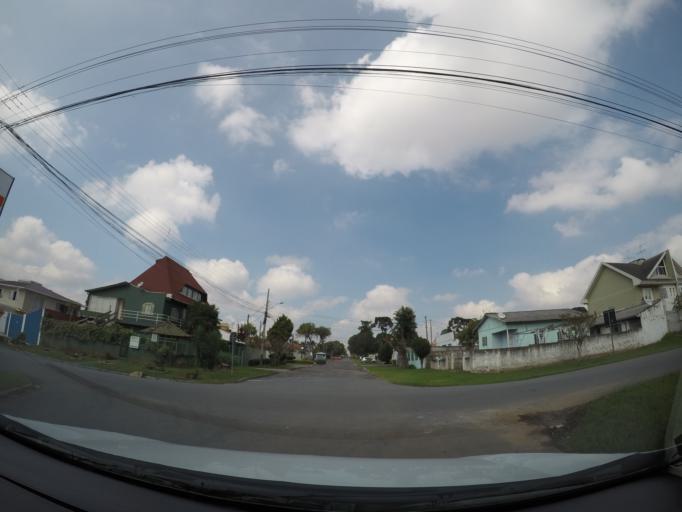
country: BR
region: Parana
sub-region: Curitiba
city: Curitiba
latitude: -25.4813
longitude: -49.2585
